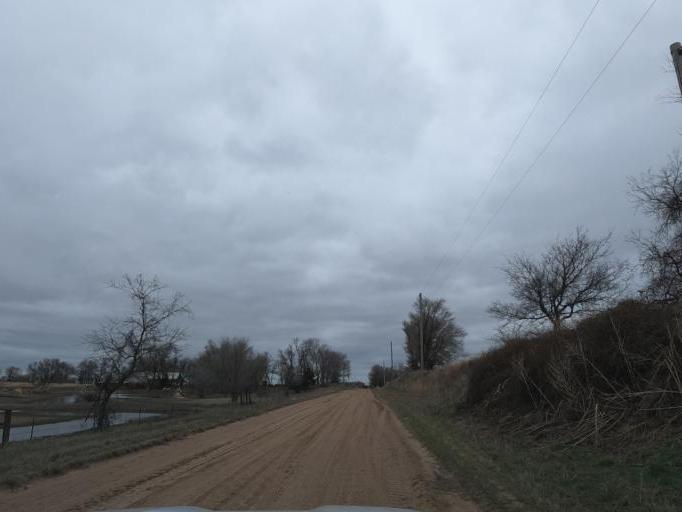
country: US
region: Kansas
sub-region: Rice County
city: Sterling
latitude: 37.9800
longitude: -98.3073
